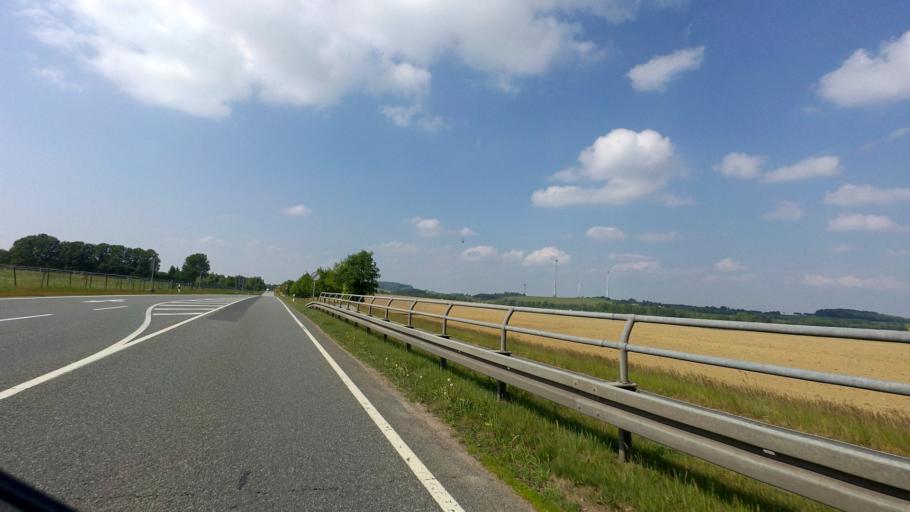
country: DE
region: Saxony
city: Lobau
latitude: 51.1128
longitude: 14.6469
